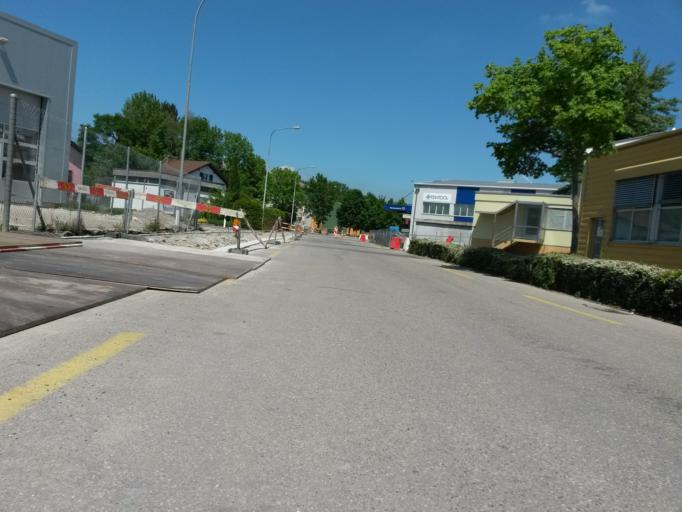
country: CH
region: Bern
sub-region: Seeland District
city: Lyss
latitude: 47.0853
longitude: 7.3036
